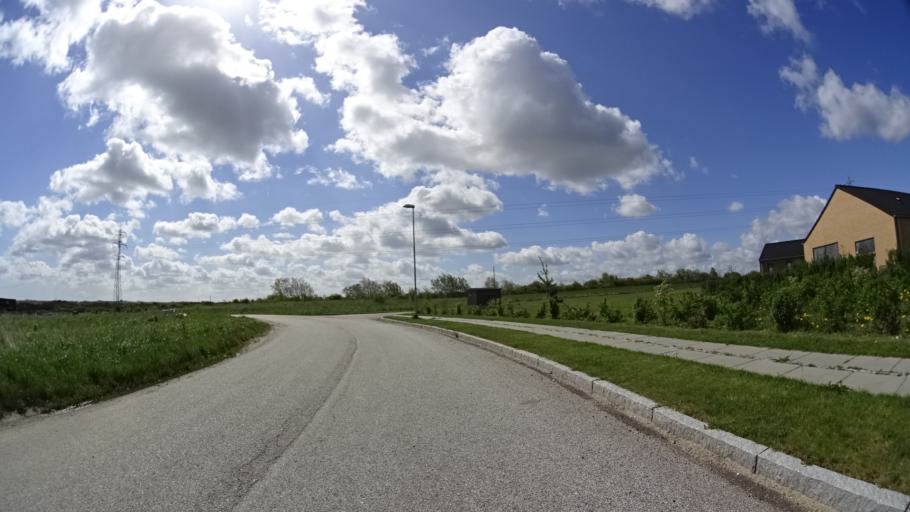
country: DK
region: Central Jutland
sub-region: Arhus Kommune
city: Stavtrup
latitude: 56.1264
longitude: 10.1114
